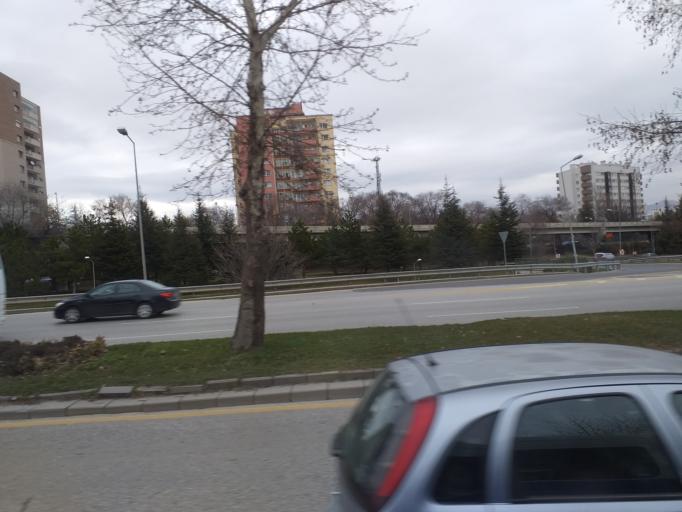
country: TR
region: Ankara
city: Ankara
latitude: 39.9555
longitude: 32.8195
